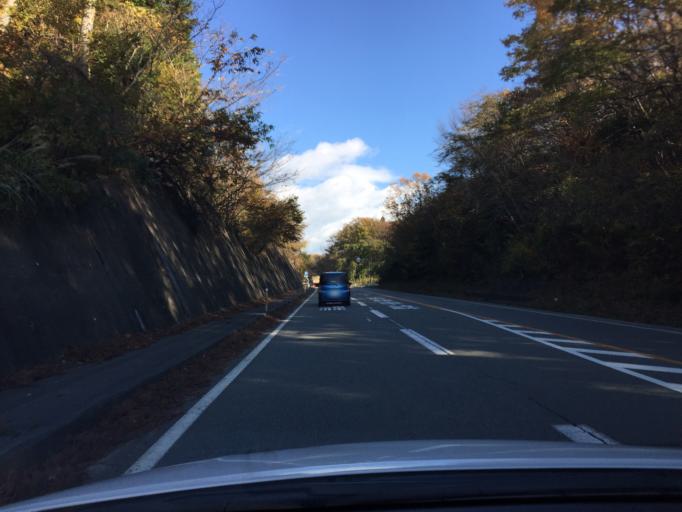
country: JP
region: Fukushima
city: Namie
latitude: 37.2916
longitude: 140.9929
